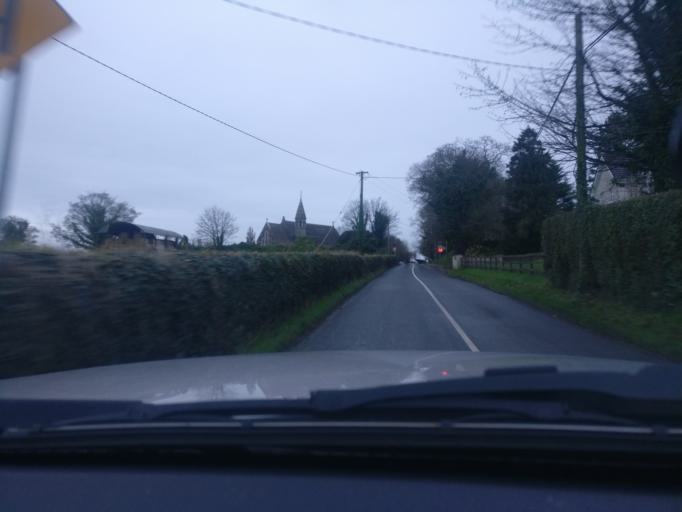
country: IE
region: Leinster
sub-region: An Mhi
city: Dunshaughlin
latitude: 53.4918
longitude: -6.6056
